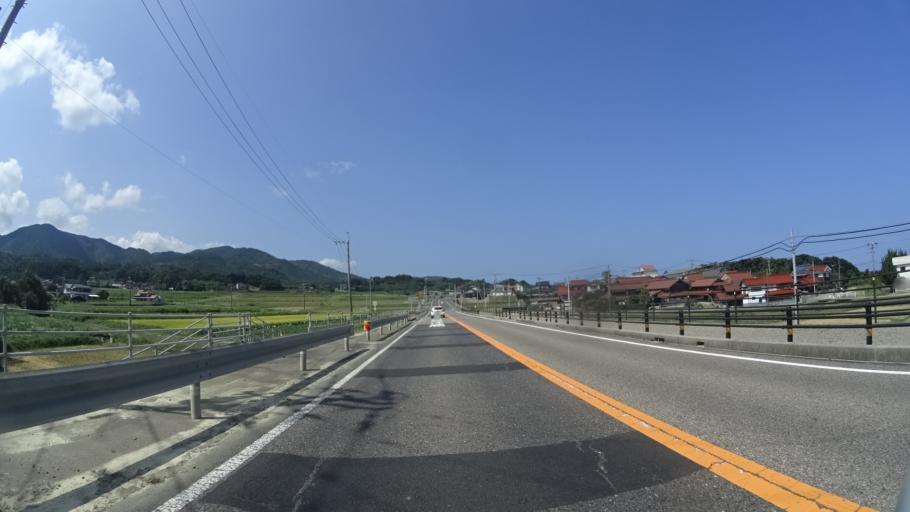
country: JP
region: Shimane
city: Masuda
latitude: 34.6709
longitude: 131.7446
